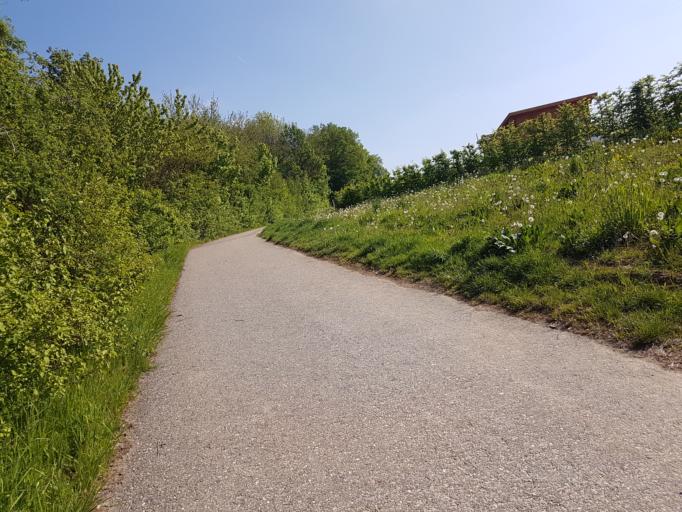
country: DE
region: Baden-Wuerttemberg
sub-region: Regierungsbezirk Stuttgart
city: Ludwigsburg
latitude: 48.8862
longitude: 9.1755
